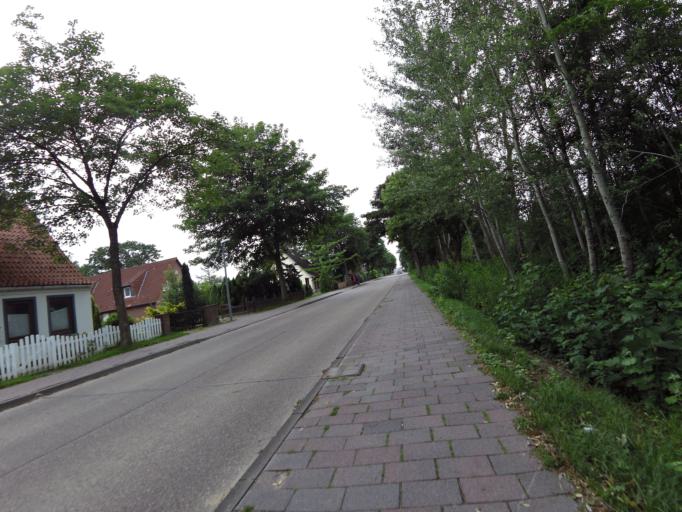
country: DE
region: Lower Saxony
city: Padingbuttel
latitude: 53.7341
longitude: 8.5235
